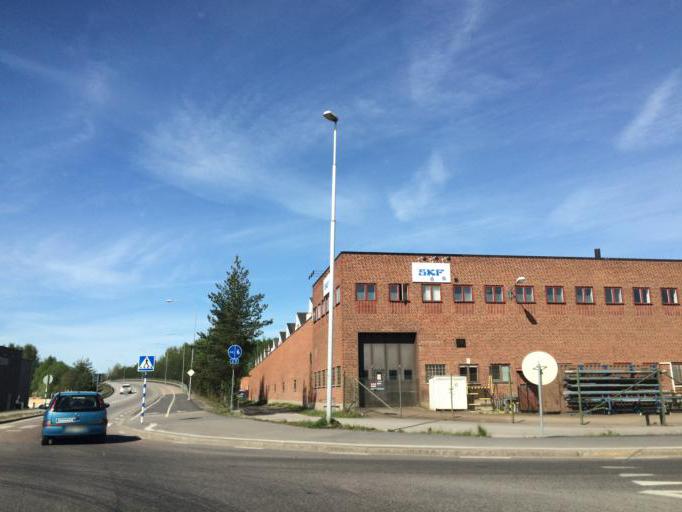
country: SE
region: Soedermanland
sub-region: Katrineholms Kommun
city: Katrineholm
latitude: 58.9962
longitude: 16.1889
